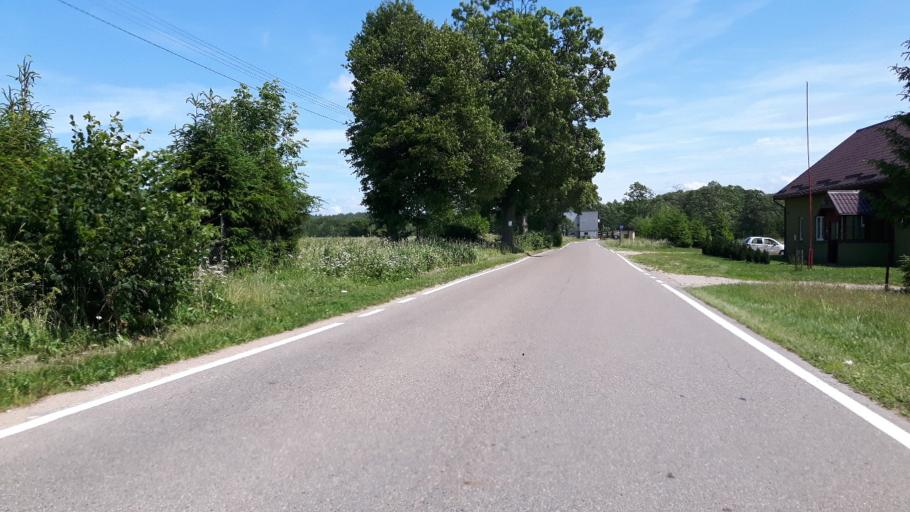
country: PL
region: Pomeranian Voivodeship
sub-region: Powiat wejherowski
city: Gniewino
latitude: 54.7247
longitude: 17.9747
